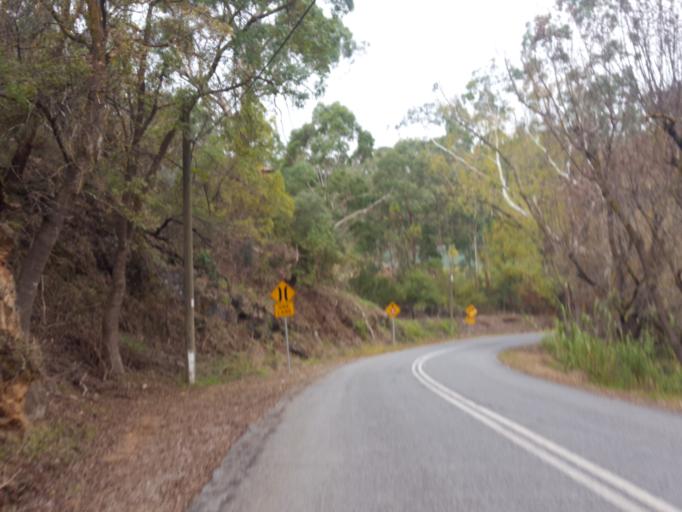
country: AU
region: South Australia
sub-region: Campbelltown
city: Athelstone
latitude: -34.8765
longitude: 138.7557
